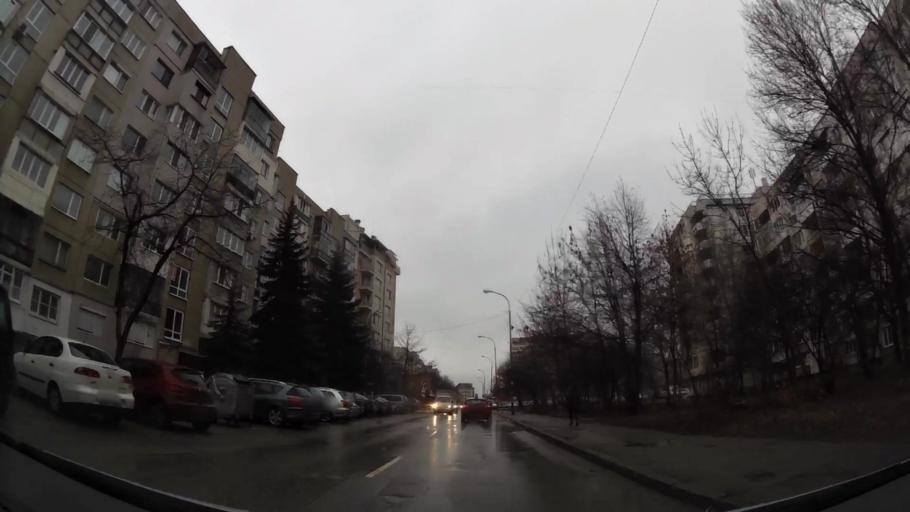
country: BG
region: Sofia-Capital
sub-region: Stolichna Obshtina
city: Sofia
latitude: 42.6418
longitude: 23.3707
